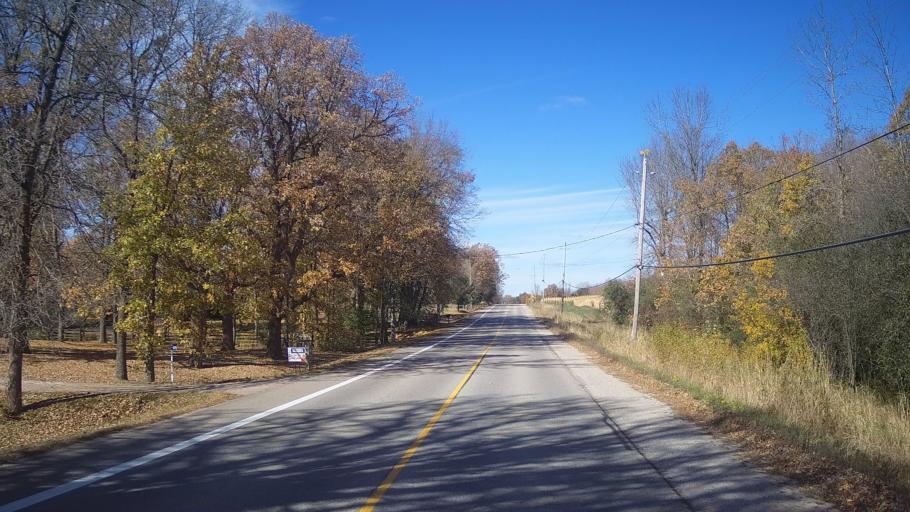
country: CA
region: Ontario
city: Perth
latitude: 44.8665
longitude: -76.2880
